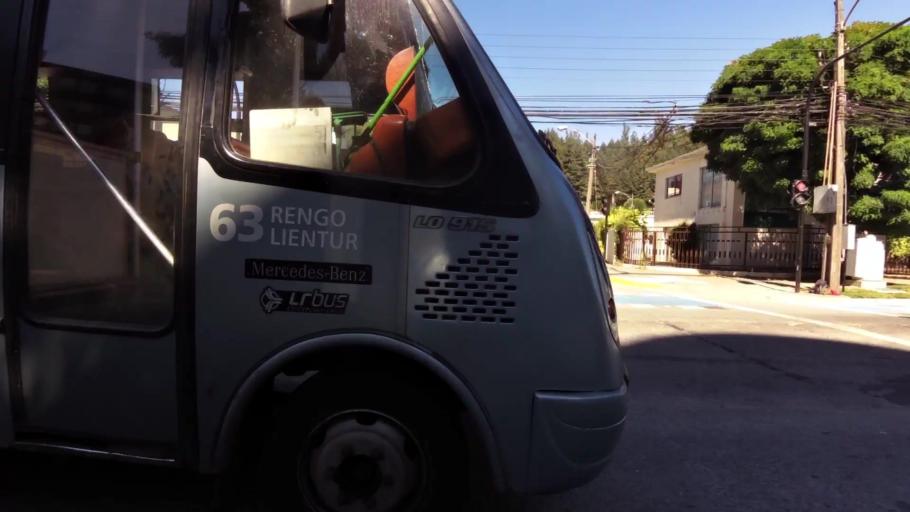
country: CL
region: Biobio
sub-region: Provincia de Concepcion
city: Concepcion
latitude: -36.8220
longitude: -73.0361
